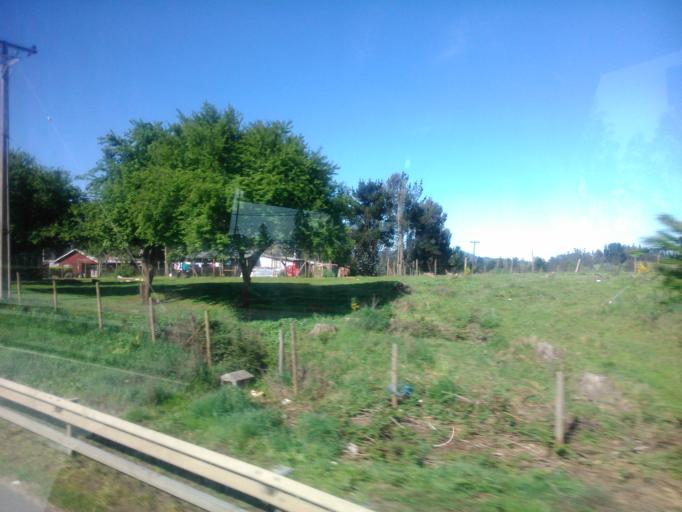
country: CL
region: Araucania
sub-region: Provincia de Cautin
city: Temuco
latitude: -38.8003
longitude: -72.6238
